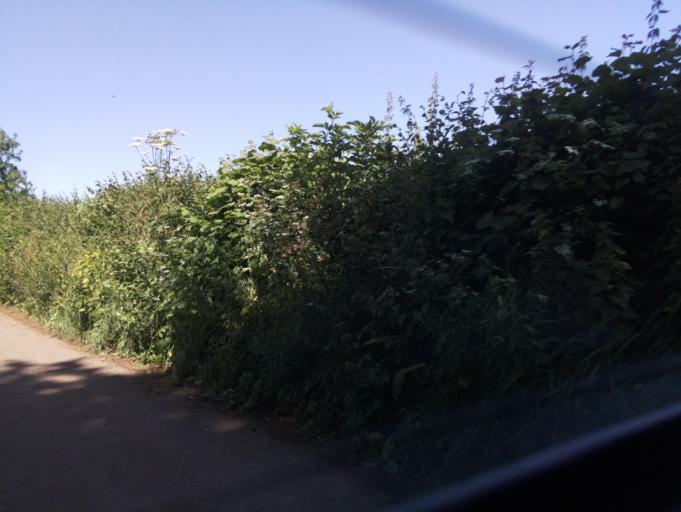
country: GB
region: England
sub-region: Devon
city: Marldon
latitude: 50.4765
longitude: -3.6017
